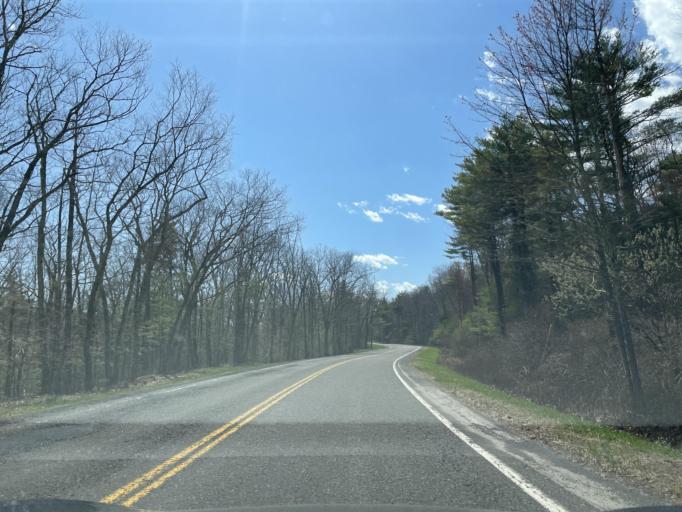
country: US
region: New York
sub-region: Ulster County
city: Woodstock
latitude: 42.0606
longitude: -74.0795
